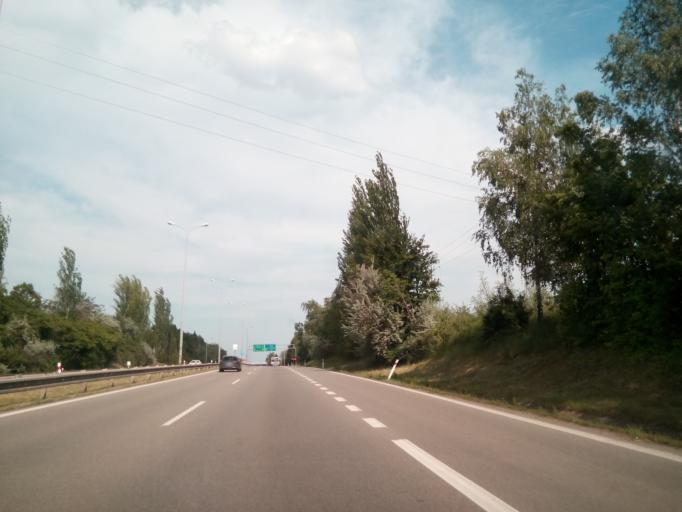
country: CZ
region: South Moravian
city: Podoli
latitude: 49.1844
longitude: 16.6836
